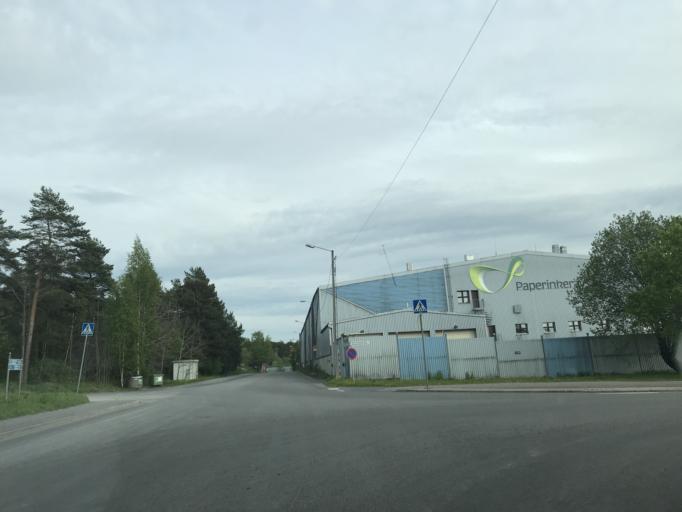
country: FI
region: Varsinais-Suomi
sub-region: Turku
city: Turku
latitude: 60.4461
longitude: 22.3101
